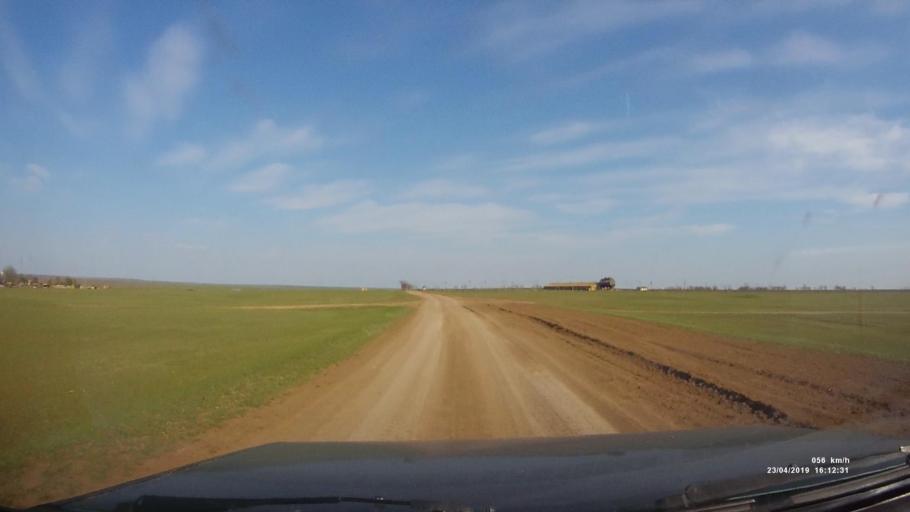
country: RU
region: Kalmykiya
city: Priyutnoye
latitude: 46.4660
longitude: 43.1271
